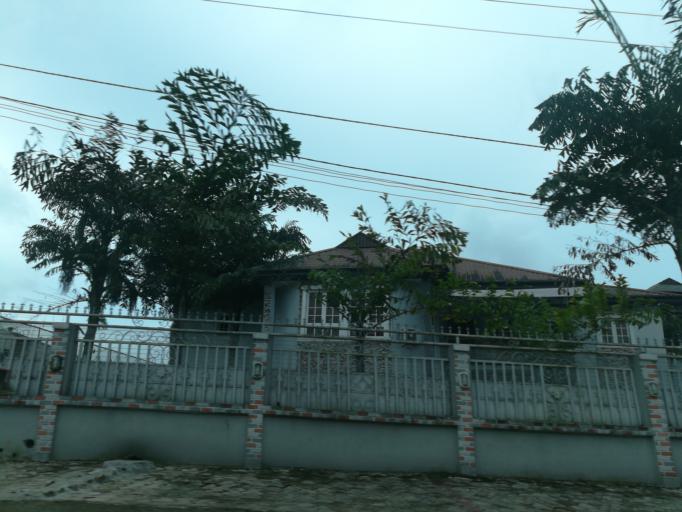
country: NG
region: Rivers
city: Port Harcourt
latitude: 4.8196
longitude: 6.9892
